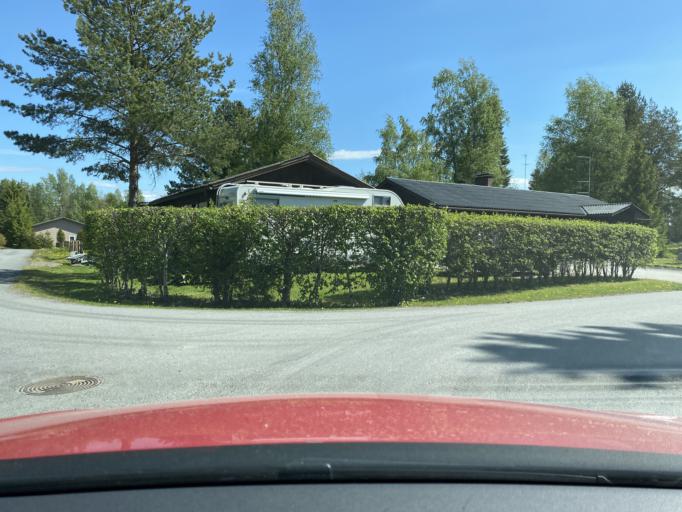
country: FI
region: Satakunta
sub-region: Rauma
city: Eura
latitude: 61.1115
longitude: 22.1322
